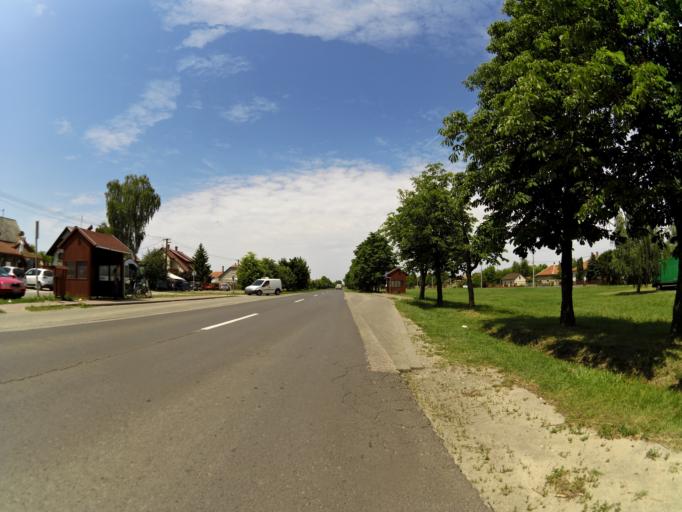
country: HU
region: Csongrad
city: Opusztaszer
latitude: 46.4946
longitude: 20.0648
